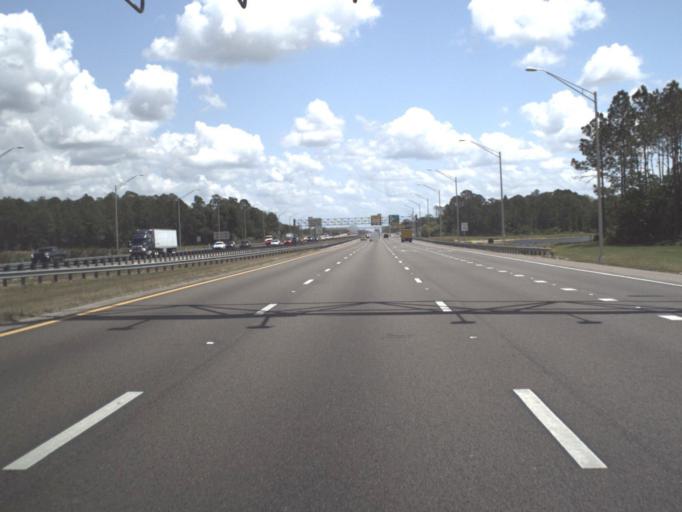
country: US
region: Florida
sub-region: Orange County
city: Alafaya
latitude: 28.4514
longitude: -81.2207
